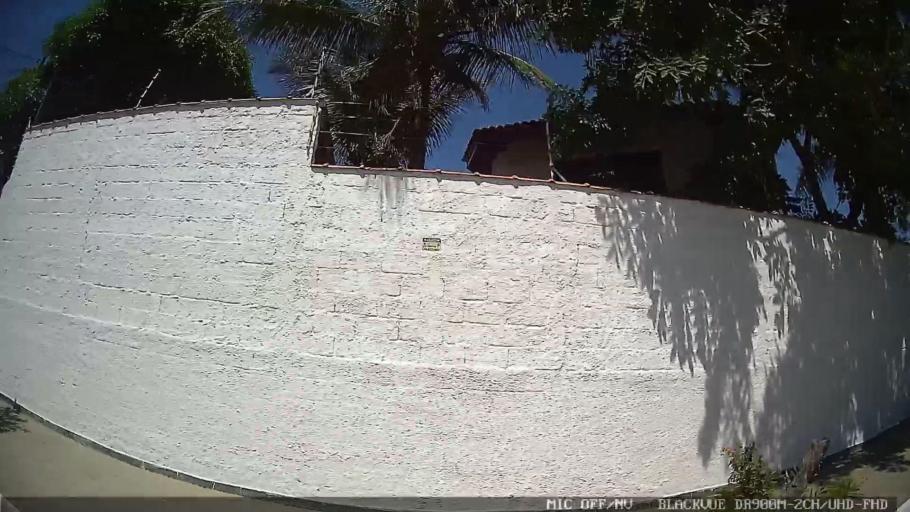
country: BR
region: Sao Paulo
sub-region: Peruibe
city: Peruibe
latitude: -24.3055
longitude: -46.9966
